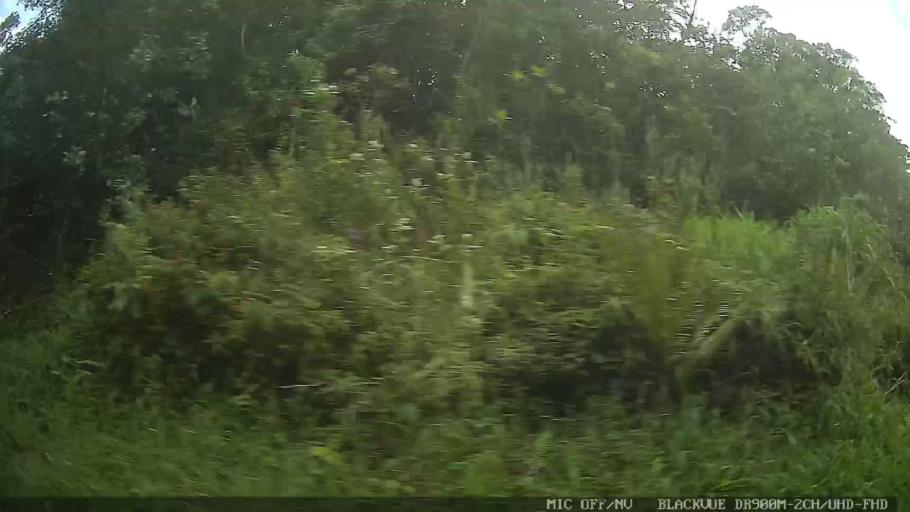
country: BR
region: Sao Paulo
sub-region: Biritiba-Mirim
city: Biritiba Mirim
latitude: -23.7087
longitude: -46.0639
